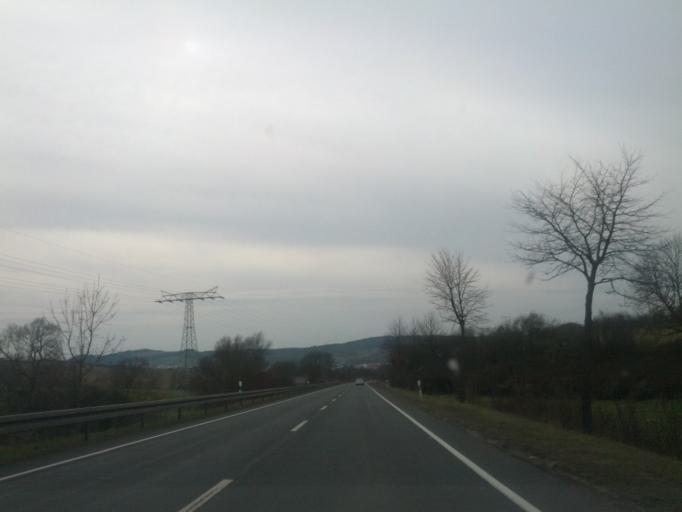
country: DE
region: Thuringia
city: Eisenach
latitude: 50.9968
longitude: 10.3438
